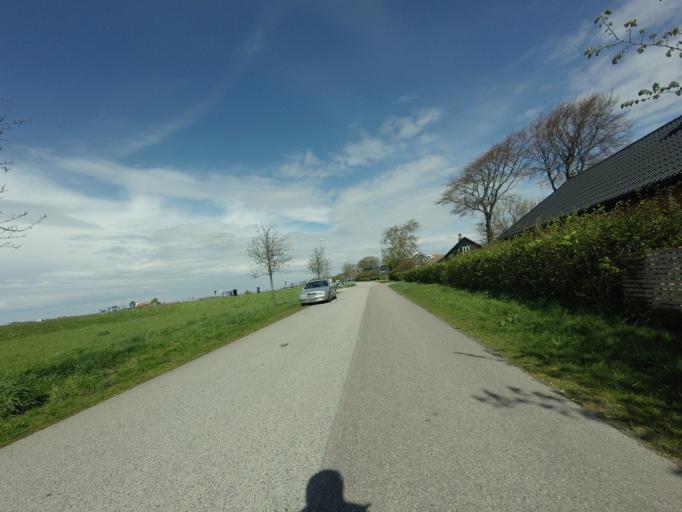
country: SE
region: Skane
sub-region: Vellinge Kommun
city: Vellinge
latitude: 55.4881
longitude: 13.0100
